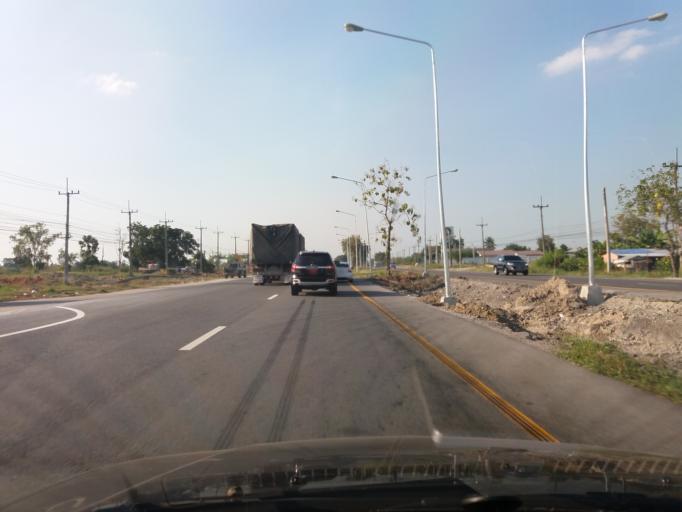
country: TH
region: Nakhon Sawan
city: Banphot Phisai
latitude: 15.8162
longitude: 99.9429
